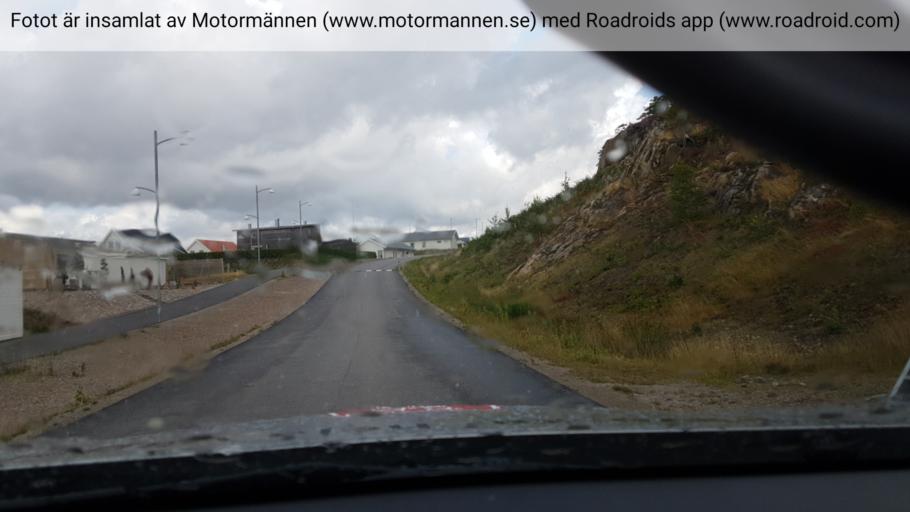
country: SE
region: Vaestra Goetaland
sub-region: Uddevalla Kommun
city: Uddevalla
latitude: 58.3205
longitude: 11.8743
